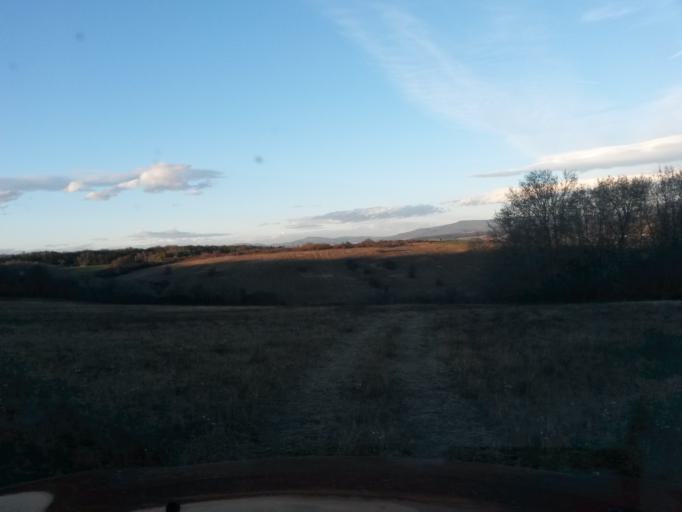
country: SK
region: Kosicky
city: Kosice
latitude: 48.7019
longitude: 21.3078
